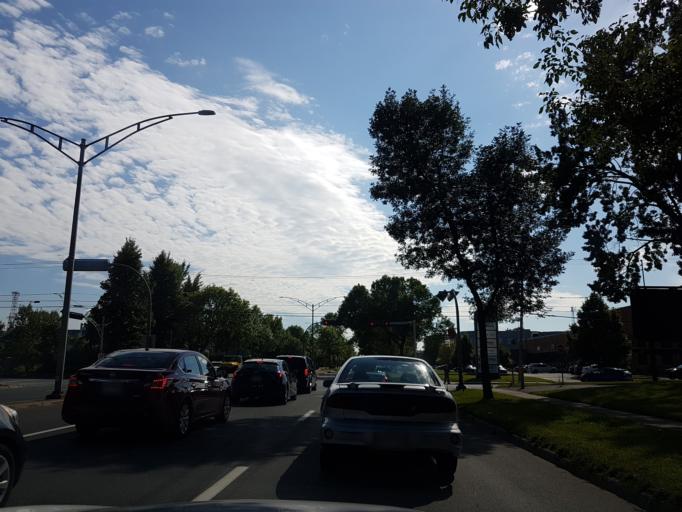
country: CA
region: Quebec
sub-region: Mauricie
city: Trois-Rivieres
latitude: 46.3314
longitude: -72.5543
